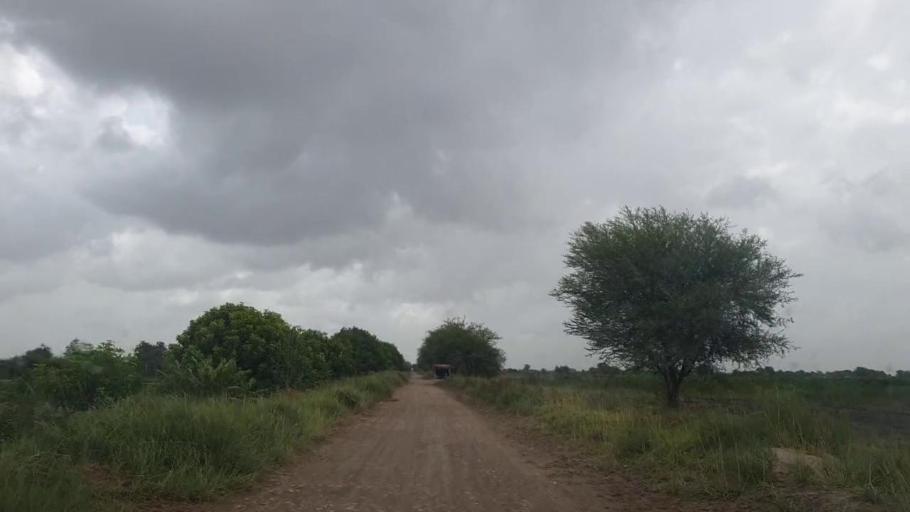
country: PK
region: Sindh
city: Naukot
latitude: 24.8474
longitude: 69.1813
